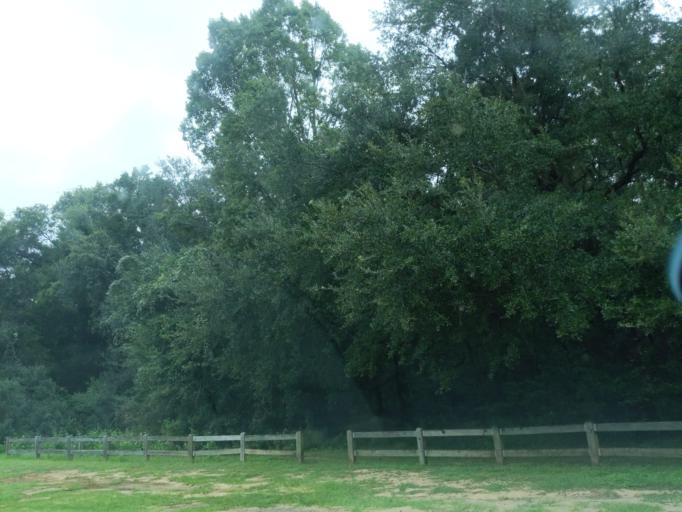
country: US
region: Florida
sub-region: Leon County
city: Tallahassee
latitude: 30.4480
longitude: -84.2121
